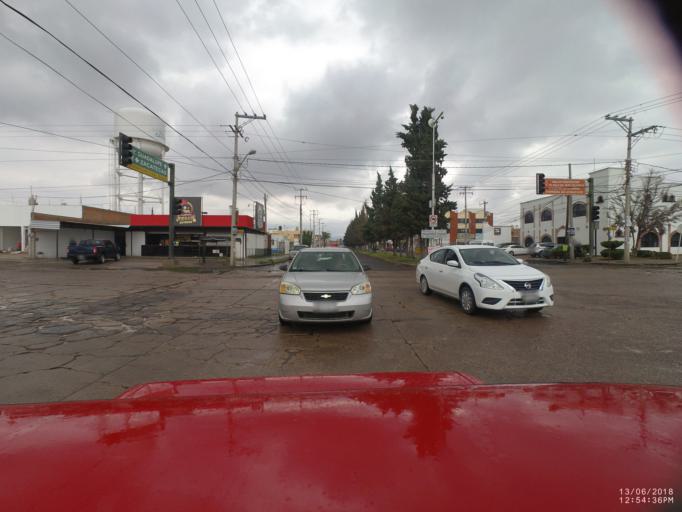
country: MX
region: Aguascalientes
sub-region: Jesus Maria
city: Arboledas Paso Blanco [Fraccionamiento]
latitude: 21.9668
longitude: -102.2934
